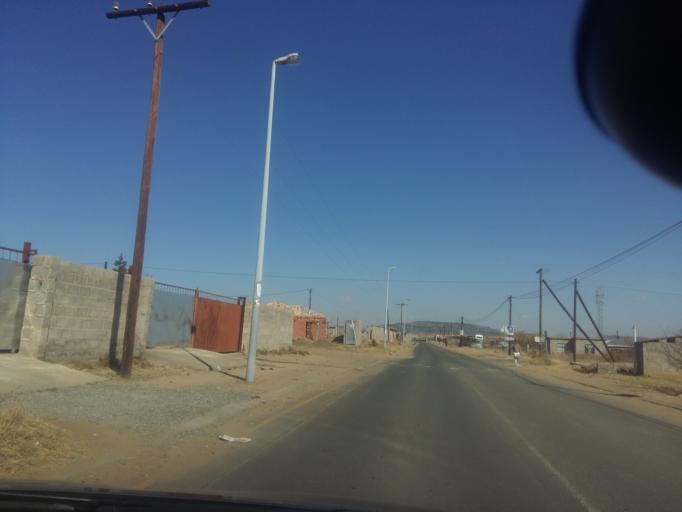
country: LS
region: Maseru
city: Maseru
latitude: -29.3401
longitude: 27.4425
